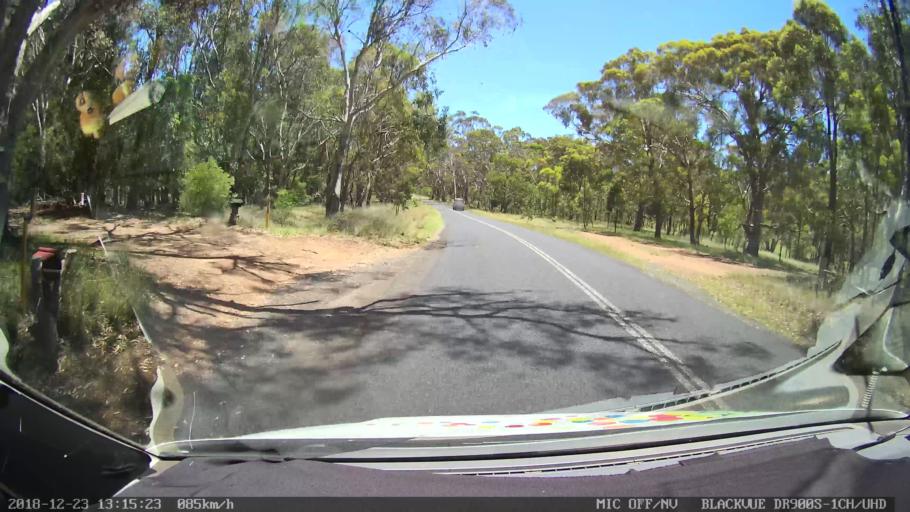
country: AU
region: New South Wales
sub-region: Armidale Dumaresq
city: Armidale
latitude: -30.5034
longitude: 151.5137
